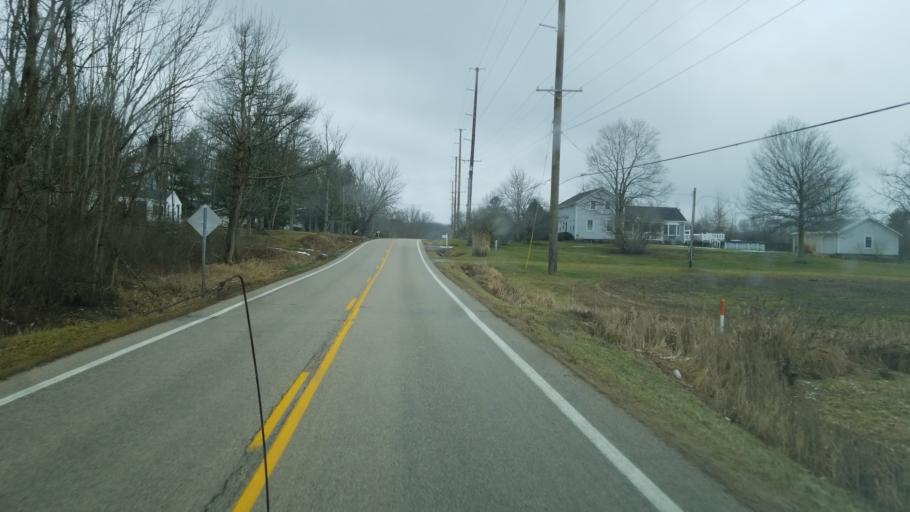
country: US
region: Ohio
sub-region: Portage County
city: Windham
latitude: 41.3085
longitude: -80.9853
